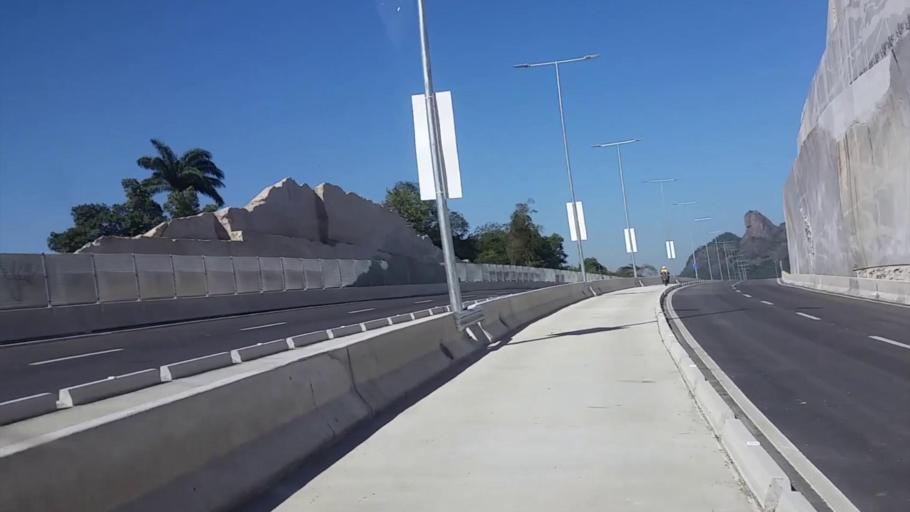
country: BR
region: Rio de Janeiro
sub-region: Nilopolis
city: Nilopolis
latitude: -22.9216
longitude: -43.3972
